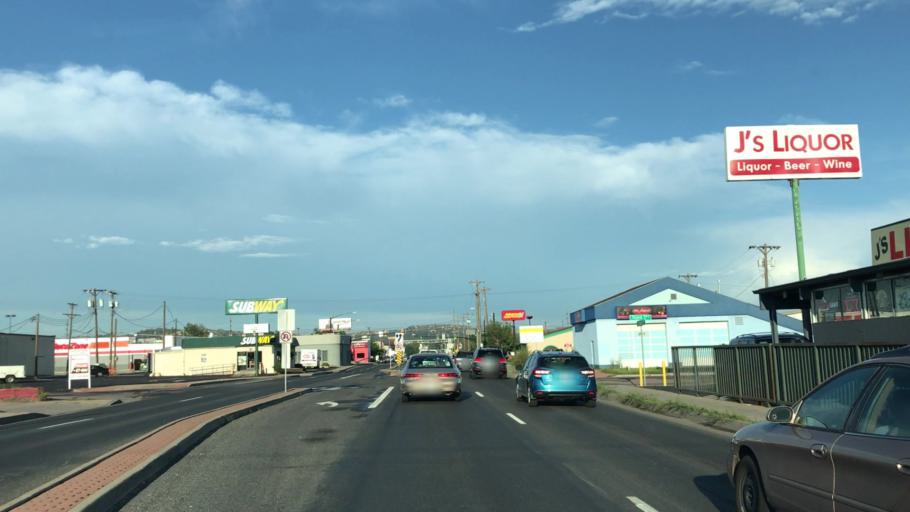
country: US
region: Colorado
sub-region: El Paso County
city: Colorado Springs
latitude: 38.8745
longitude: -104.8219
